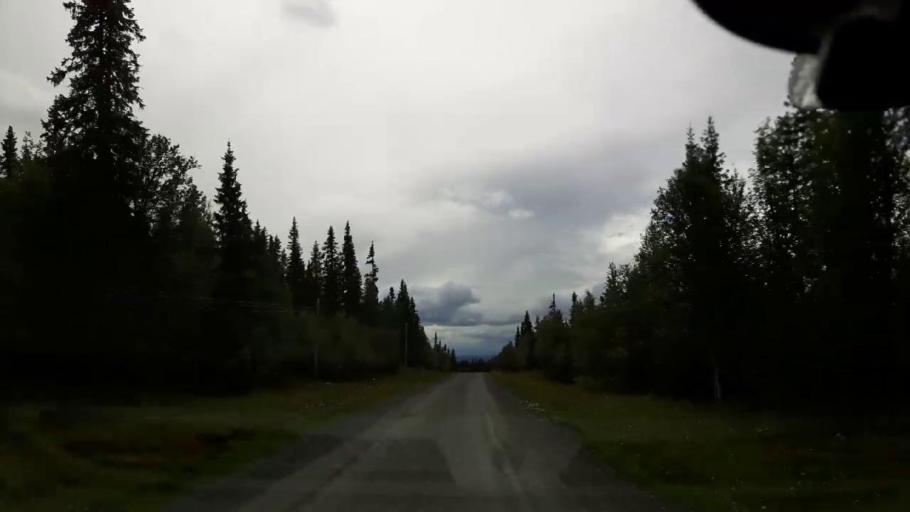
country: SE
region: Jaemtland
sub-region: Krokoms Kommun
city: Valla
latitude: 63.7629
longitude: 13.8374
